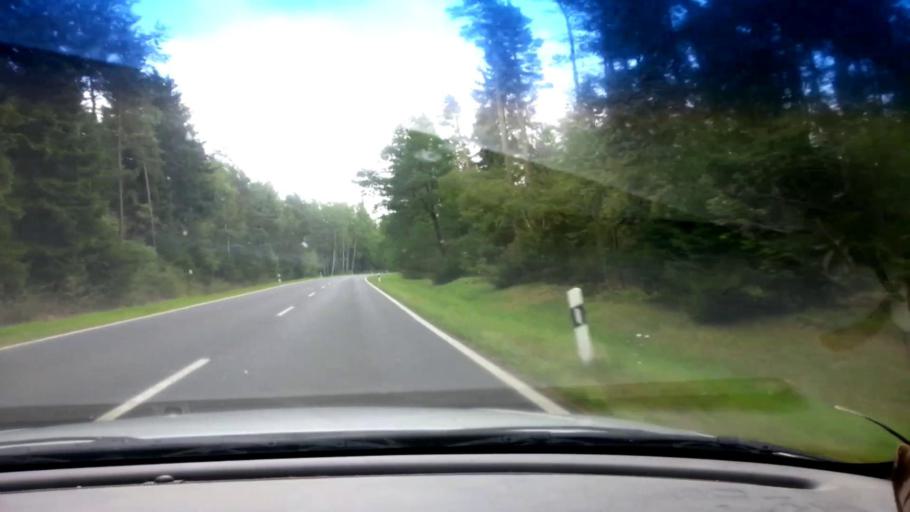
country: DE
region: Bavaria
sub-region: Upper Franconia
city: Schirnding
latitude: 50.0736
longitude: 12.2379
